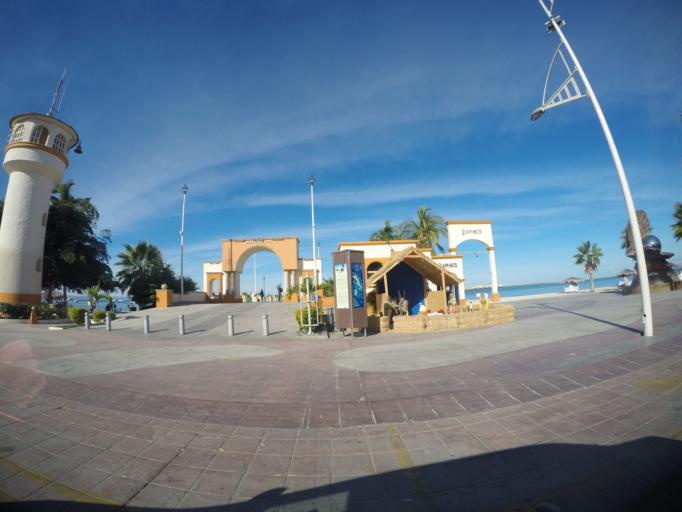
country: MX
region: Baja California Sur
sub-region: La Paz
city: La Paz
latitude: 24.1935
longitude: -110.2957
